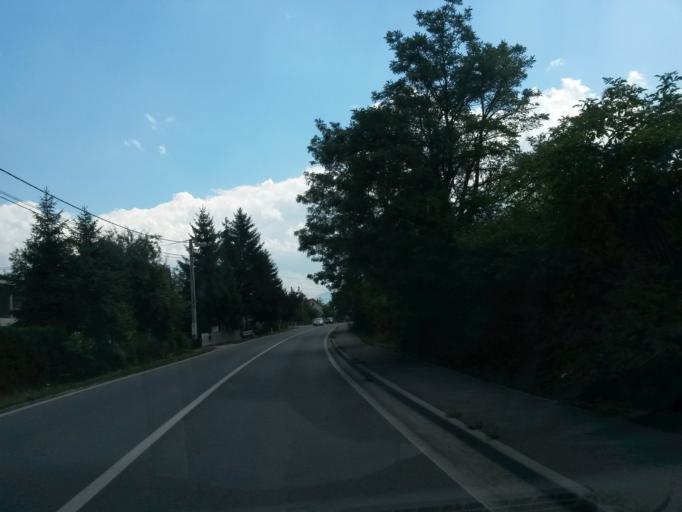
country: BA
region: Federation of Bosnia and Herzegovina
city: Travnik
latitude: 44.2007
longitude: 17.7256
